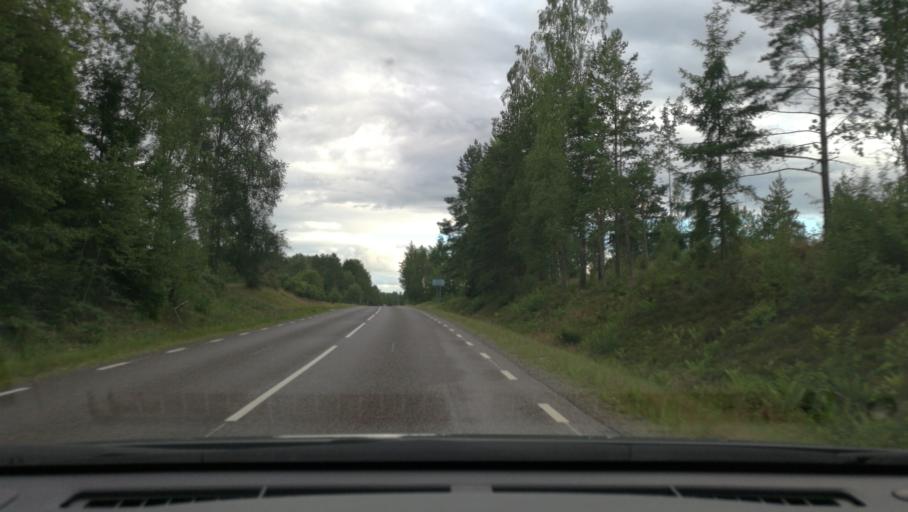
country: SE
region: OEstergoetland
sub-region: Norrkopings Kommun
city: Svartinge
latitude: 58.7225
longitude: 15.9428
